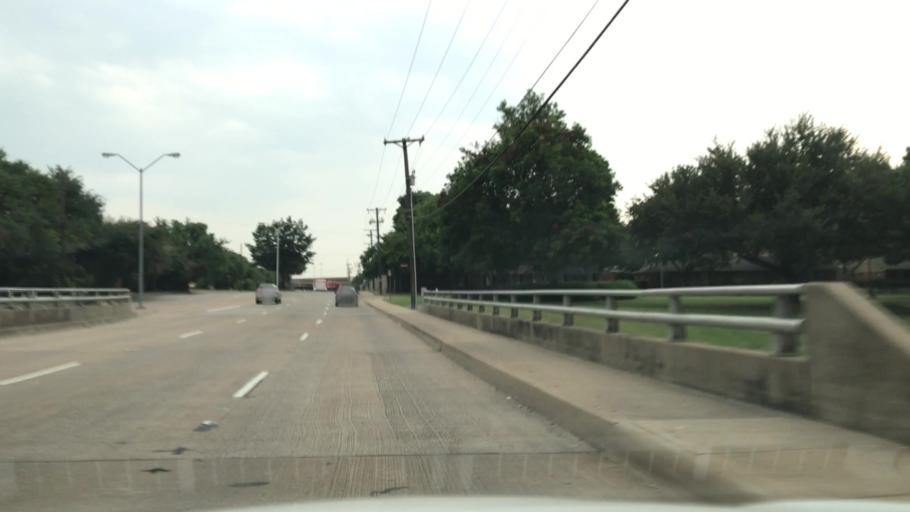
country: US
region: Texas
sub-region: Dallas County
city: Farmers Branch
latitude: 32.9158
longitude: -96.8818
